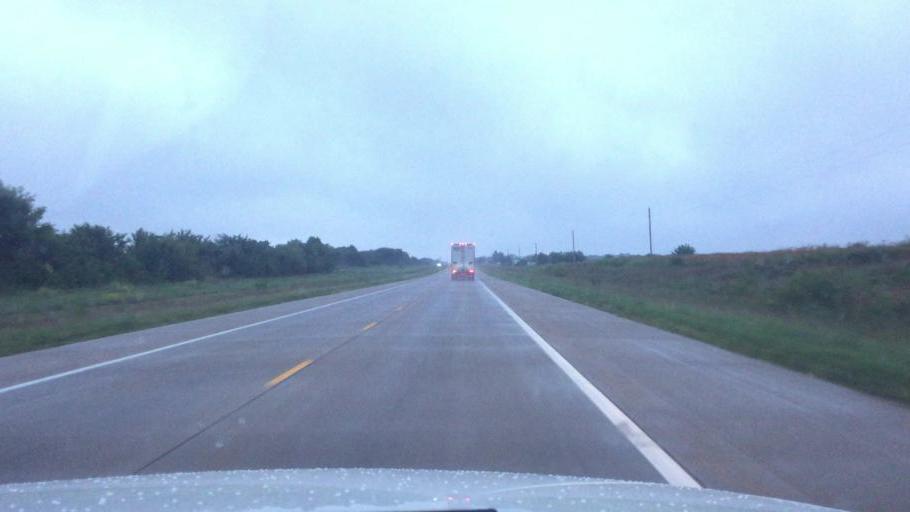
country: US
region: Kansas
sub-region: Neosho County
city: Chanute
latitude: 37.5099
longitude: -95.4709
